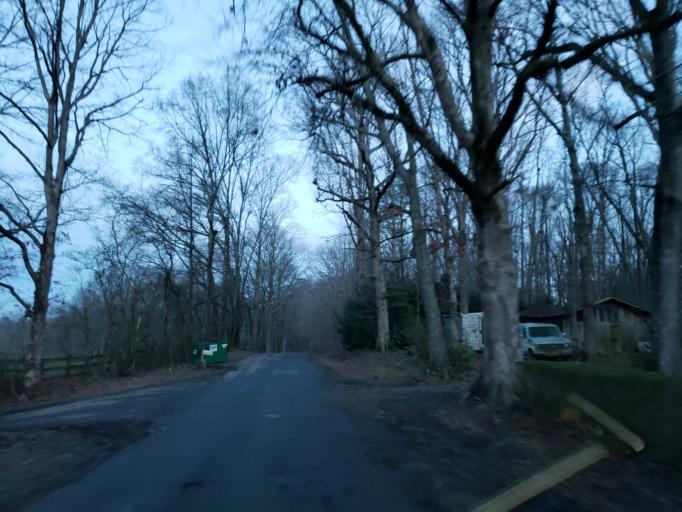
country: US
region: Georgia
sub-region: Cherokee County
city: Ball Ground
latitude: 34.2917
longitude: -84.2947
